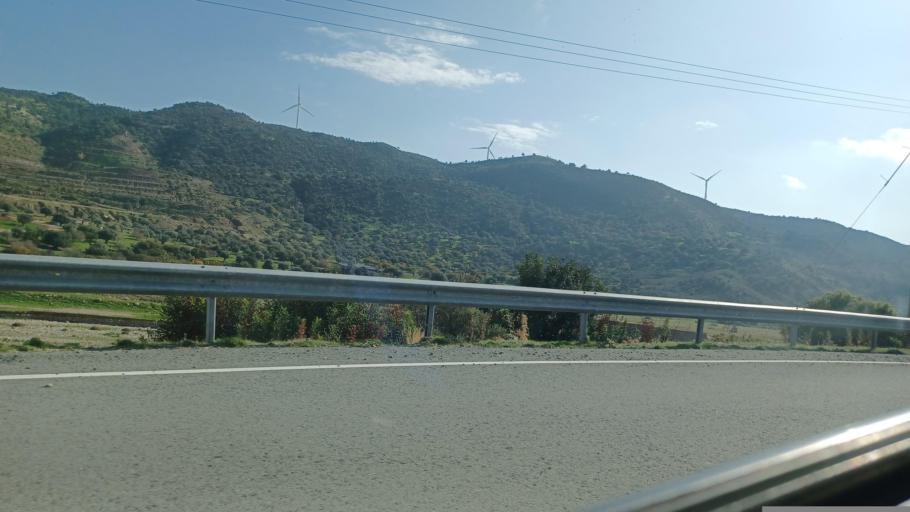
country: CY
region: Limassol
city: Pissouri
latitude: 34.7427
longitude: 32.6064
